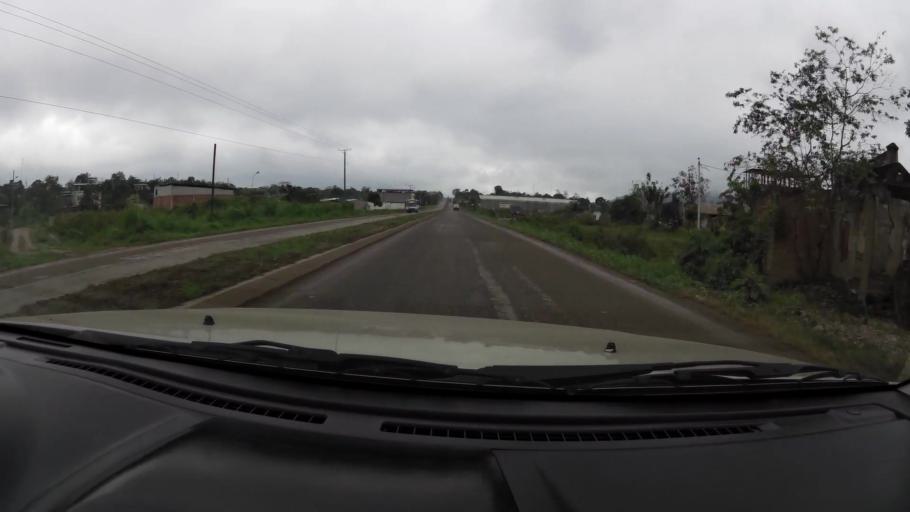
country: EC
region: El Oro
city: Pasaje
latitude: -3.3379
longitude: -79.7938
